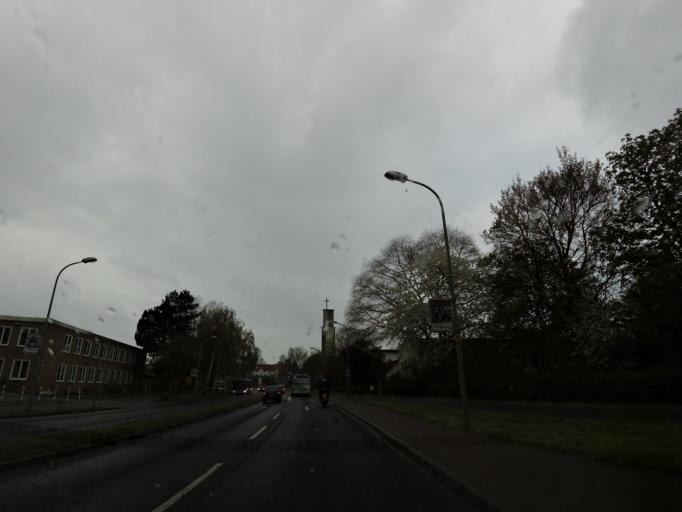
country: DE
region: Lower Saxony
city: Goettingen
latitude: 51.5414
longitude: 9.9191
